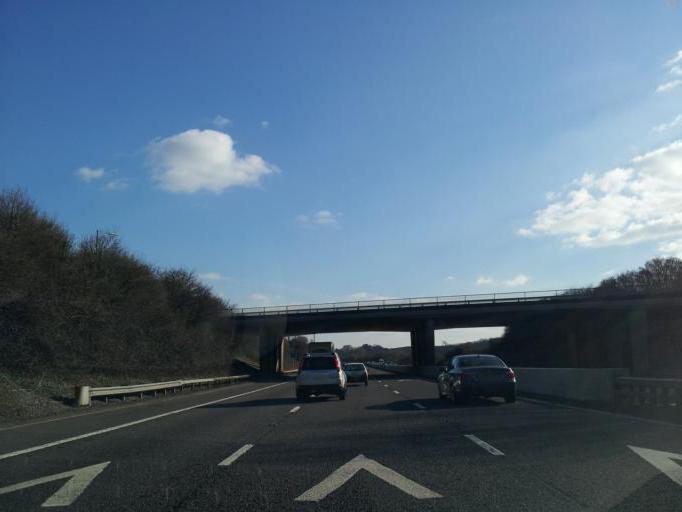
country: GB
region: England
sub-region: North Somerset
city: Banwell
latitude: 51.3312
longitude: -2.8930
